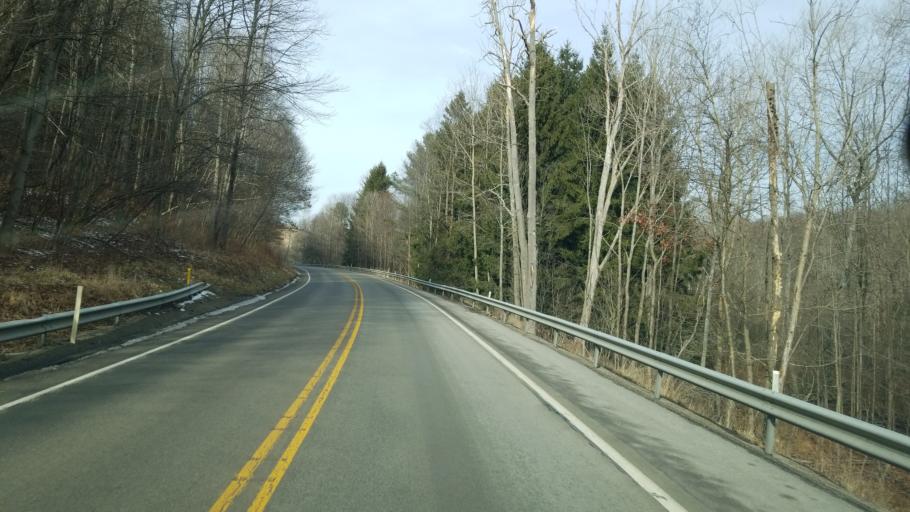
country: US
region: Pennsylvania
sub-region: Indiana County
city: Johnsonburg
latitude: 40.7971
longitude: -78.8517
